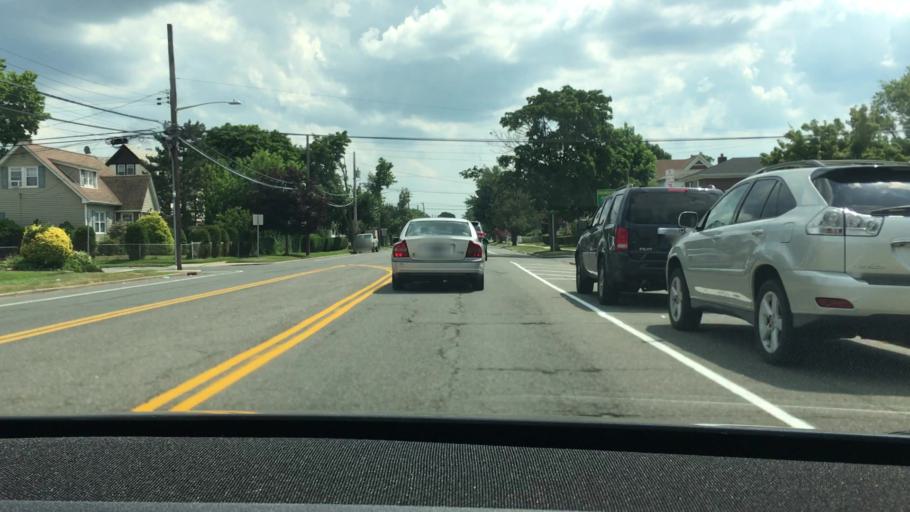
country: US
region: New York
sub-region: Nassau County
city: North Valley Stream
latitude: 40.6729
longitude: -73.6942
